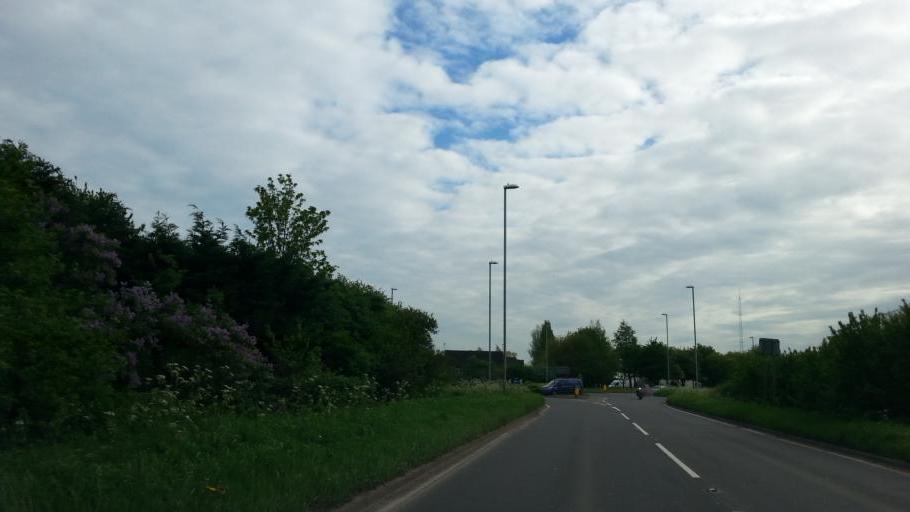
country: GB
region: England
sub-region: Cambridgeshire
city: Chatteris
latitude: 52.4529
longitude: 0.0395
